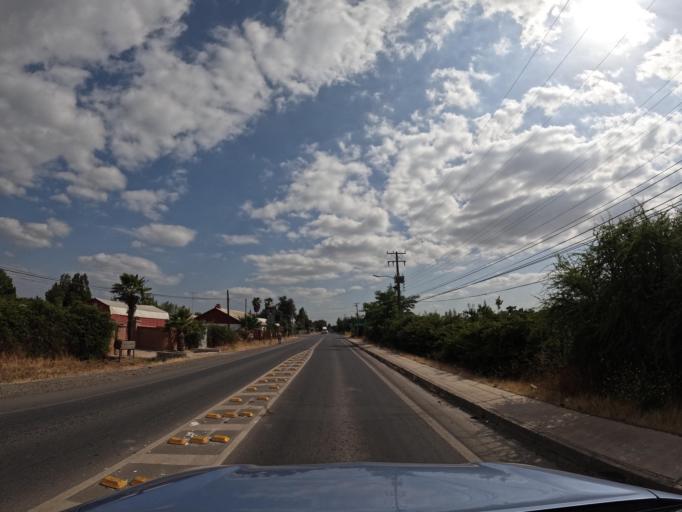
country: CL
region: Maule
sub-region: Provincia de Curico
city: Molina
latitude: -35.1434
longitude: -71.2792
